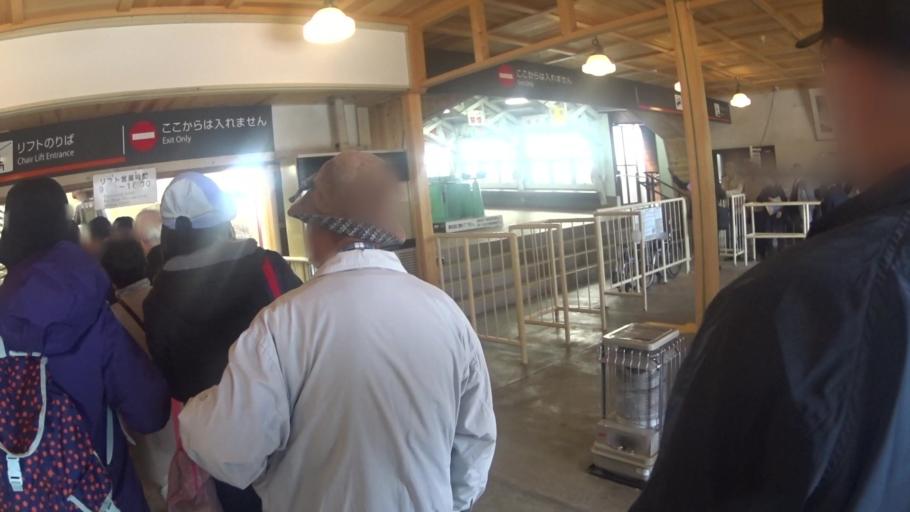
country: JP
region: Kyoto
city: Miyazu
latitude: 35.5834
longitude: 135.1951
